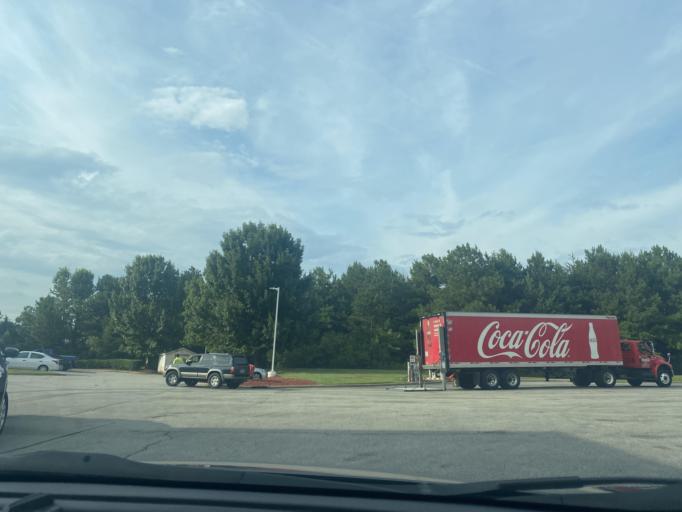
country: US
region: South Carolina
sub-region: Cherokee County
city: East Gaffney
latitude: 35.1080
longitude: -81.6052
